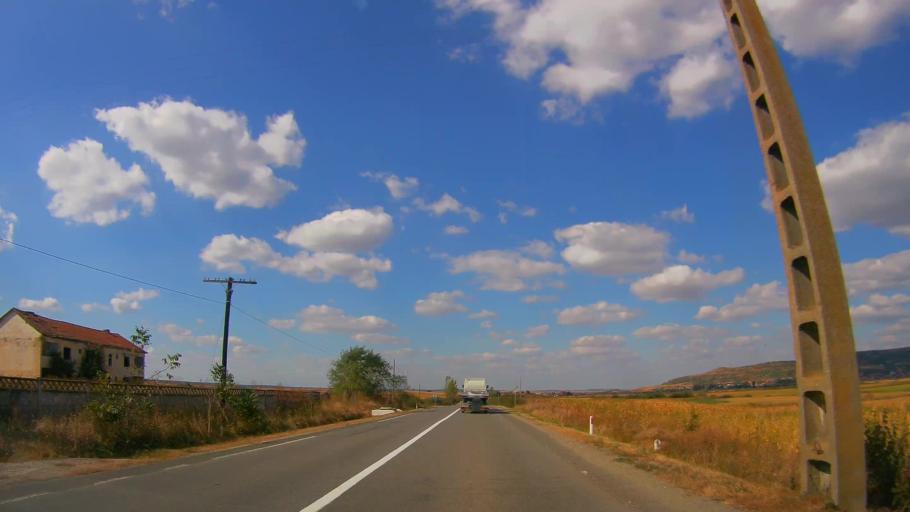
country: RO
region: Salaj
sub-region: Comuna Bobota
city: Dersida
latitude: 47.3661
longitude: 22.7915
